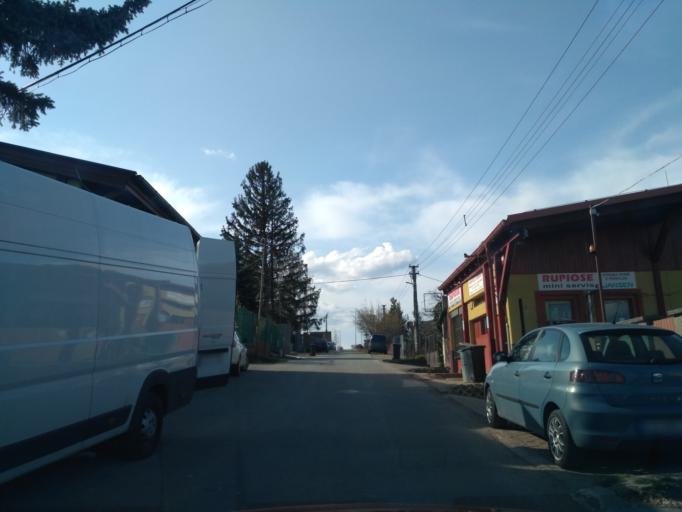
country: SK
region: Kosicky
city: Kosice
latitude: 48.6923
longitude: 21.2031
